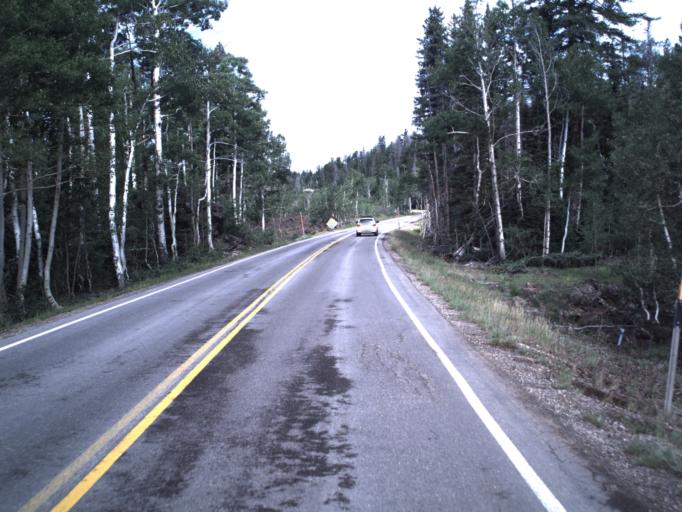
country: US
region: Utah
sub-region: Iron County
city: Parowan
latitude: 37.5239
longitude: -112.7412
